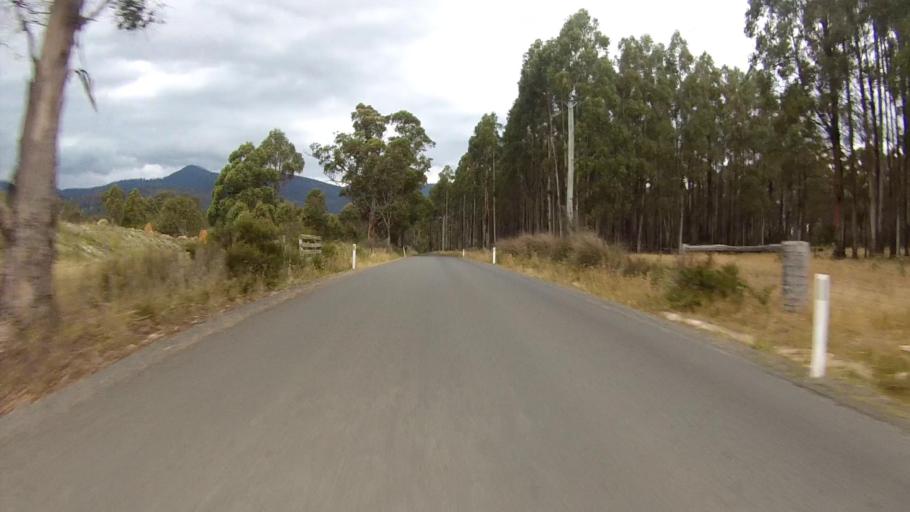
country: AU
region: Tasmania
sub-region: Huon Valley
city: Huonville
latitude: -42.9669
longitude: 147.0849
